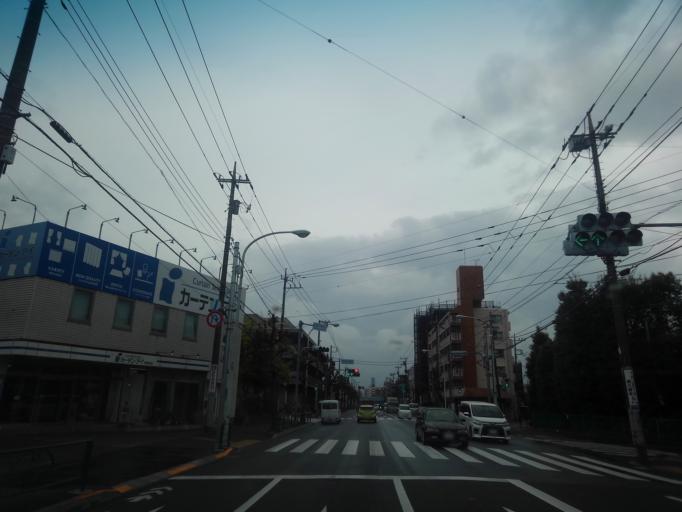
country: JP
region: Tokyo
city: Tanashicho
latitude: 35.7340
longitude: 139.5306
